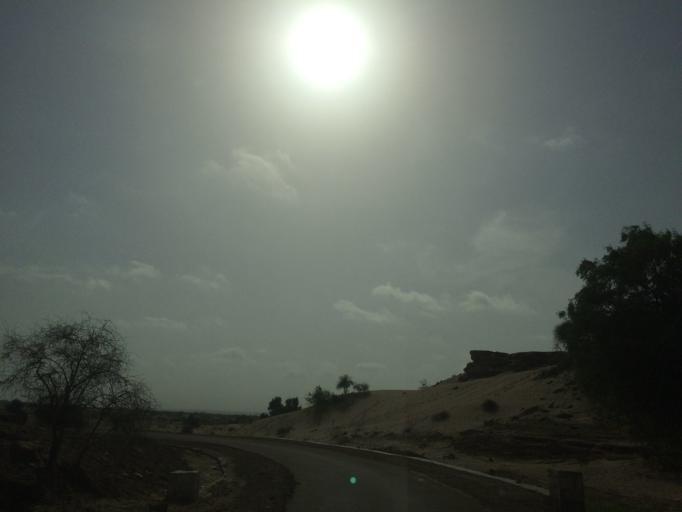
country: IN
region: Rajasthan
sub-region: Jaisalmer
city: Jaisalmer
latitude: 26.7688
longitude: 70.6830
